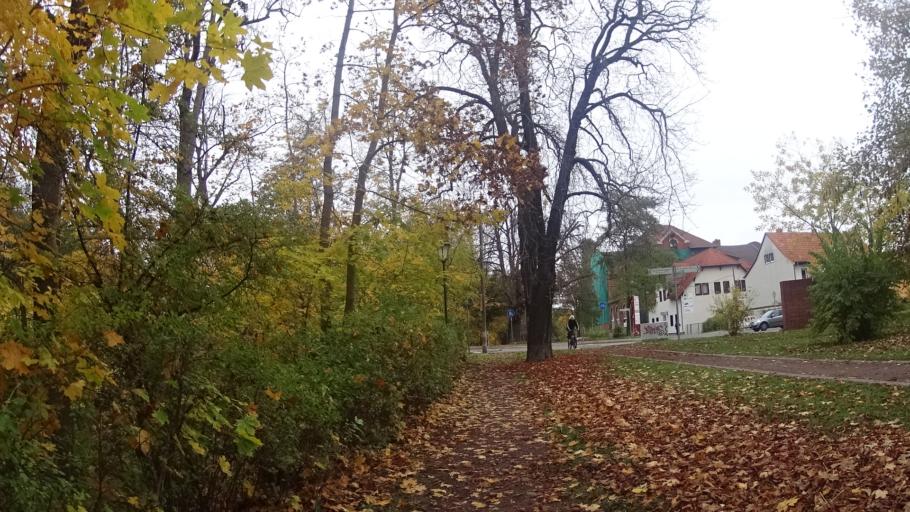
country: DE
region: Thuringia
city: Arnstadt
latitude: 50.8317
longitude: 10.9538
